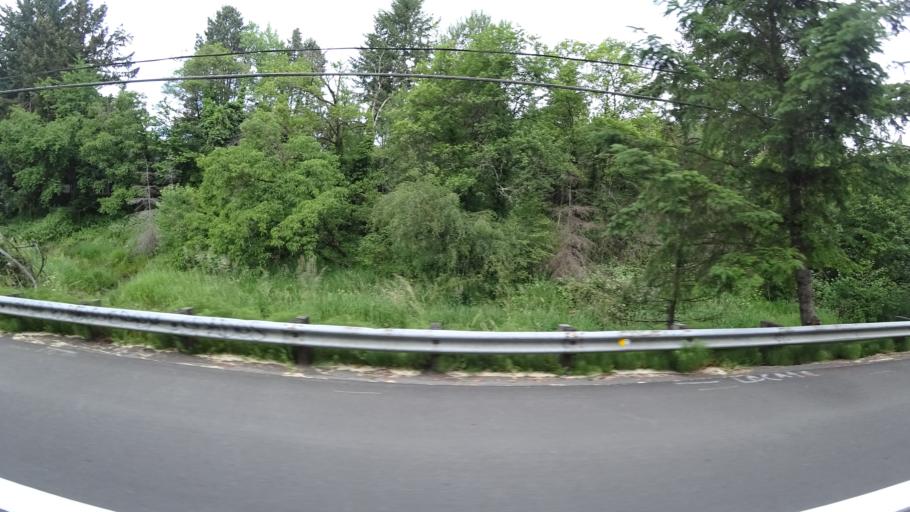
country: US
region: Oregon
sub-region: Washington County
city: Raleigh Hills
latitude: 45.4824
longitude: -122.7117
